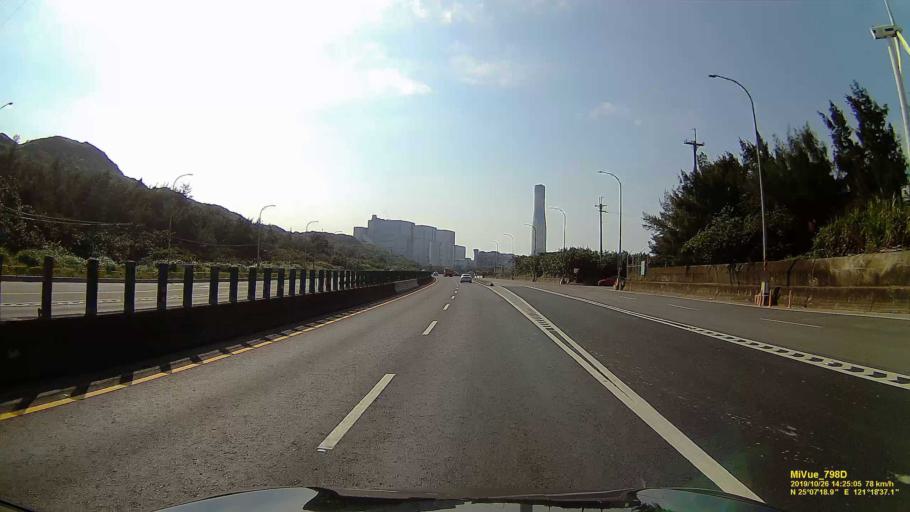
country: TW
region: Taiwan
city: Taoyuan City
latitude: 25.1219
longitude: 121.3098
